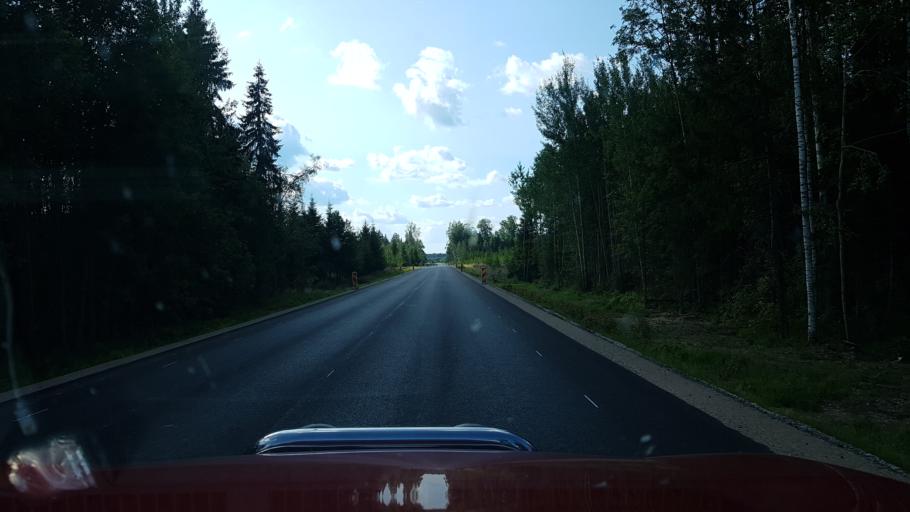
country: EE
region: Viljandimaa
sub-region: Moisakuela linn
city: Moisakula
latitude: 58.1237
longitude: 25.1712
